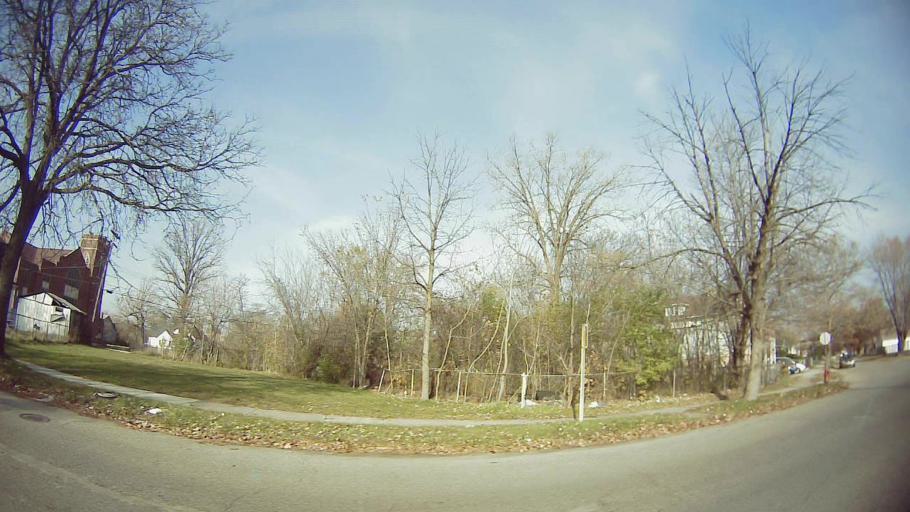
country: US
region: Michigan
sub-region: Wayne County
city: Highland Park
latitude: 42.4104
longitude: -83.1156
